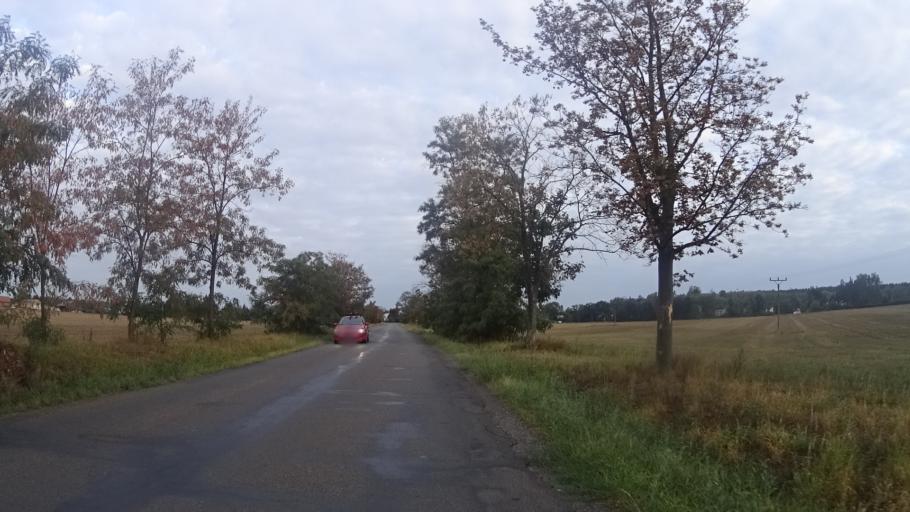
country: CZ
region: Kralovehradecky
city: Cernilov
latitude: 50.2114
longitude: 15.9143
